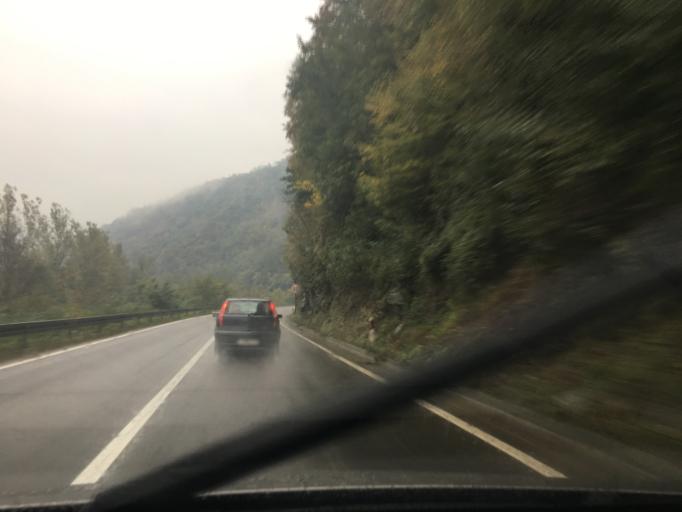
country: RS
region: Central Serbia
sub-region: Pcinjski Okrug
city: Vladicin Han
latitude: 42.7410
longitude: 22.0610
